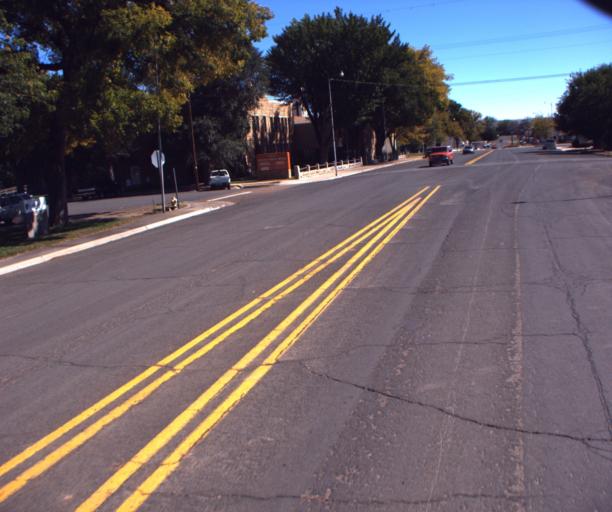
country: US
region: Arizona
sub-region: Apache County
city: Saint Johns
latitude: 34.5067
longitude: -109.3666
